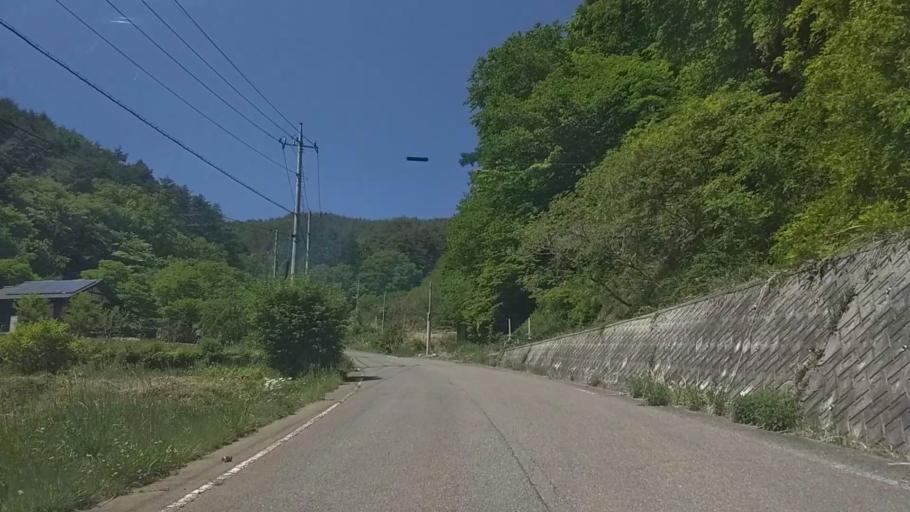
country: JP
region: Yamanashi
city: Nirasaki
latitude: 35.8605
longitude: 138.4474
